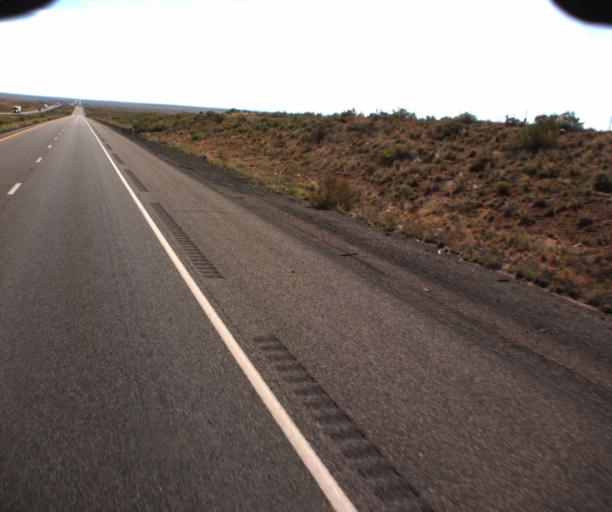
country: US
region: Arizona
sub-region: Navajo County
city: Holbrook
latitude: 35.0703
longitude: -109.7548
